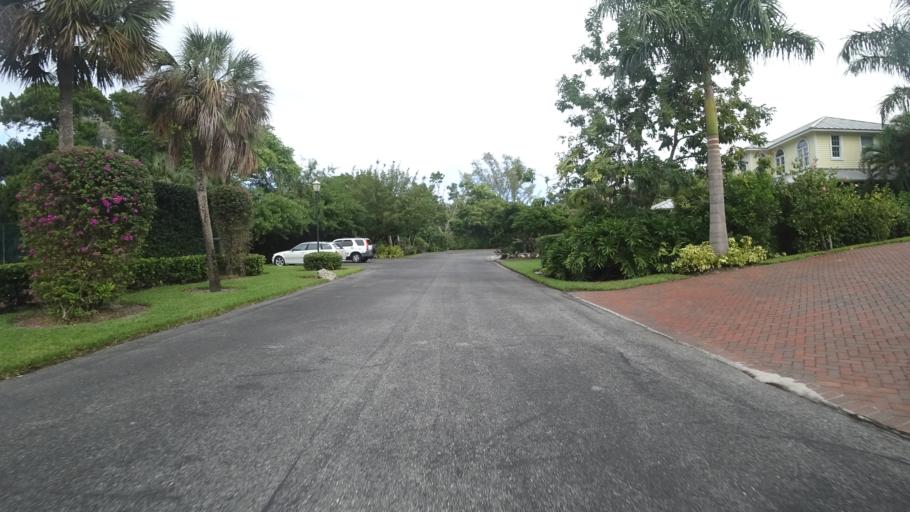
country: US
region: Florida
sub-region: Manatee County
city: Longboat Key
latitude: 27.4121
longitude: -82.6557
